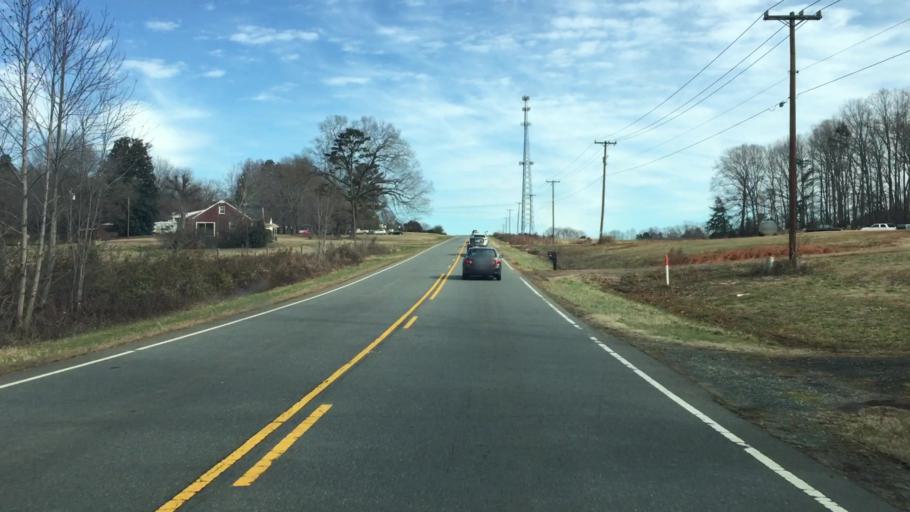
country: US
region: North Carolina
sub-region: Guilford County
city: Oak Ridge
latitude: 36.2144
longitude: -80.0630
